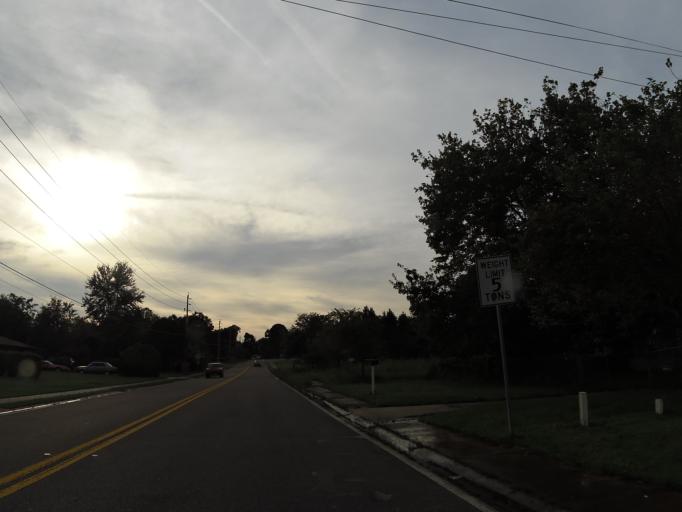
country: US
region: Florida
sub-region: Duval County
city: Jacksonville
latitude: 30.3978
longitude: -81.7176
